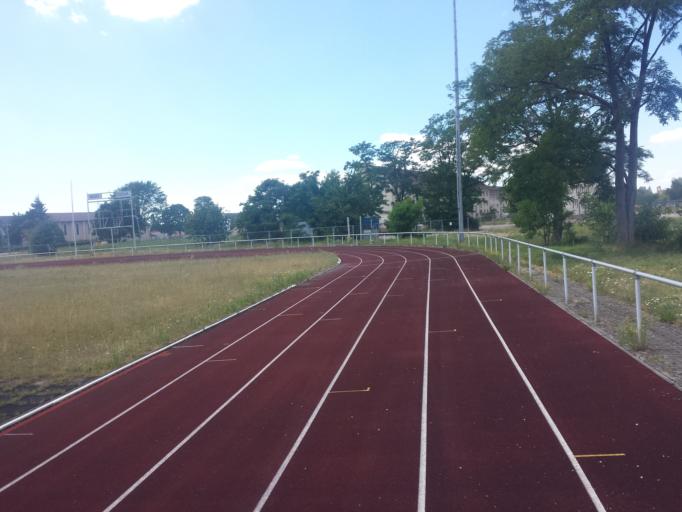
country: DE
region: Hesse
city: Viernheim
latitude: 49.5187
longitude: 8.5333
